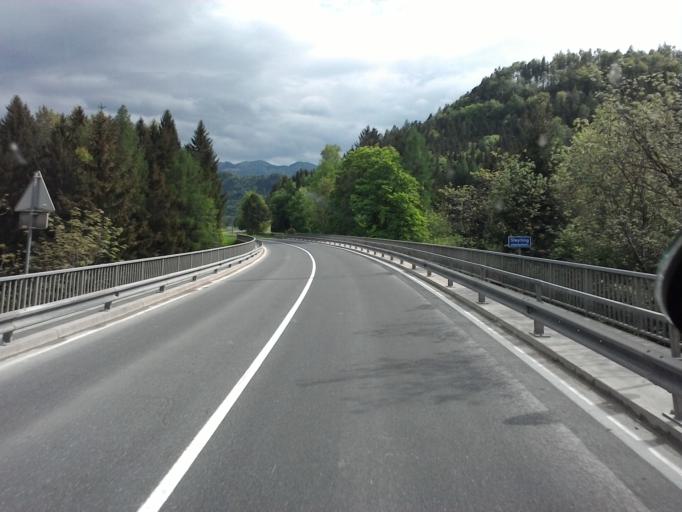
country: AT
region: Upper Austria
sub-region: Politischer Bezirk Kirchdorf an der Krems
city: Micheldorf in Oberoesterreich
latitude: 47.8042
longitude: 14.1607
